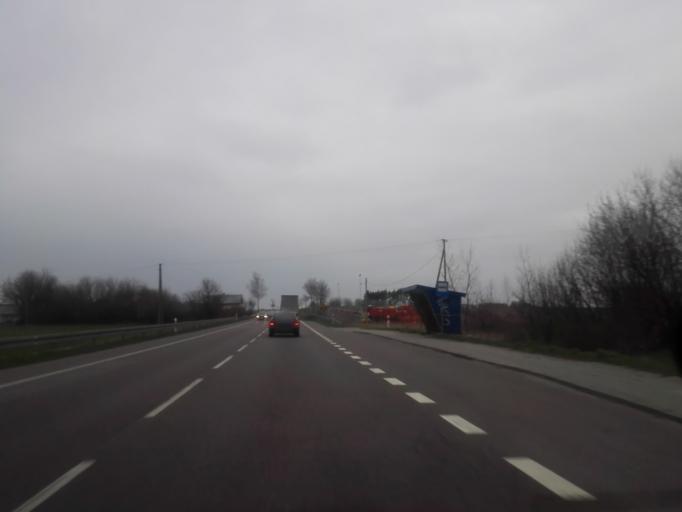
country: PL
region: Podlasie
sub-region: Powiat grajewski
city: Szczuczyn
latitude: 53.5870
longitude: 22.3295
